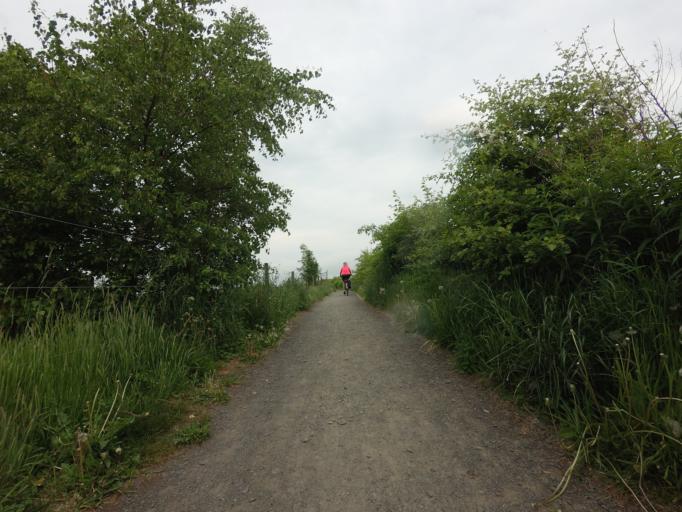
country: GB
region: Scotland
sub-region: Fife
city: Ballingry
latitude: 56.2219
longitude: -3.3541
